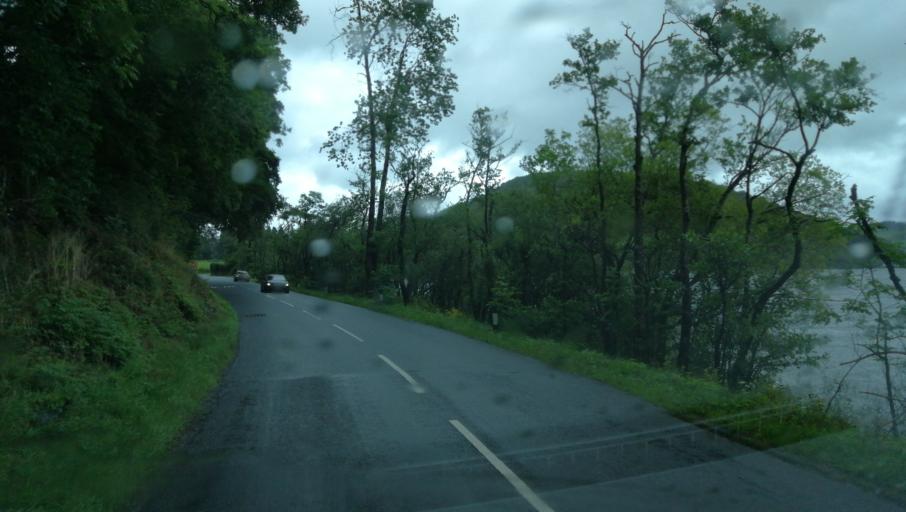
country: GB
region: England
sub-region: Cumbria
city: Penrith
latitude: 54.6089
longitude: -2.8361
